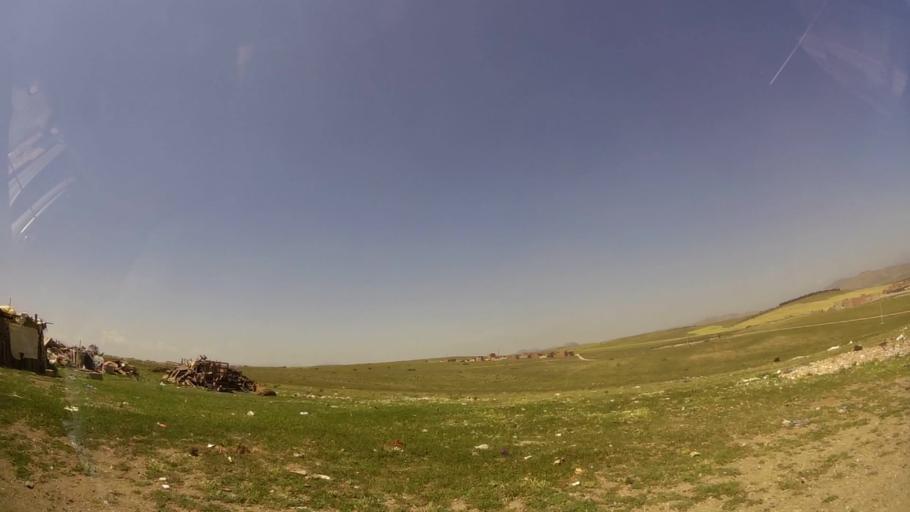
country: MA
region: Oriental
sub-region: Oujda-Angad
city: Oujda
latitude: 34.6750
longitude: -1.9550
